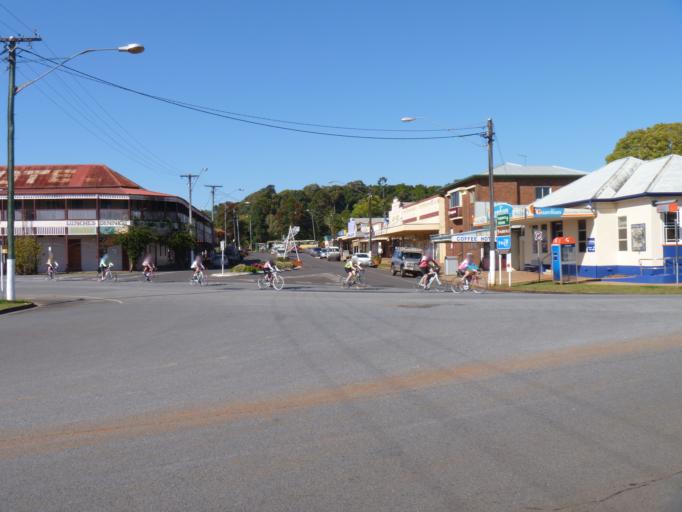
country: AU
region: Queensland
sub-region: Tablelands
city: Atherton
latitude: -17.3516
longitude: 145.5930
